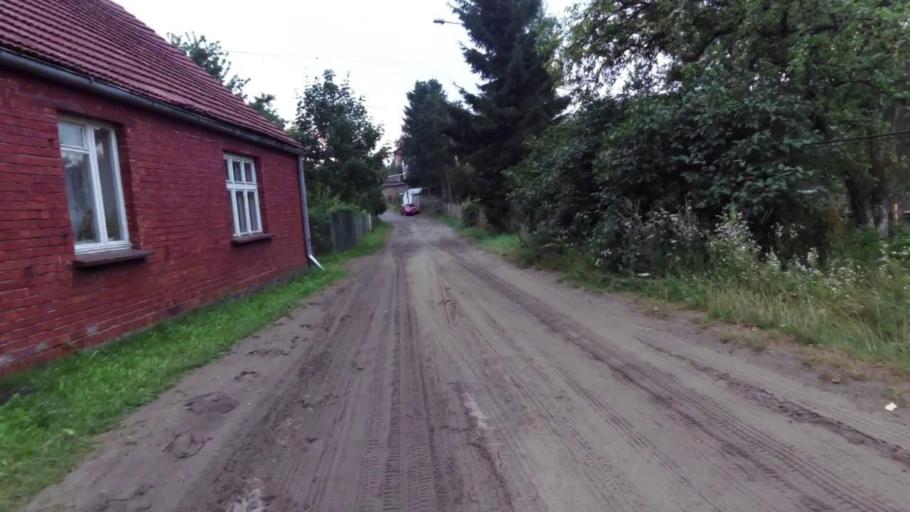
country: PL
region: West Pomeranian Voivodeship
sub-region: Powiat szczecinecki
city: Lubowo
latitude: 53.5878
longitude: 16.3872
